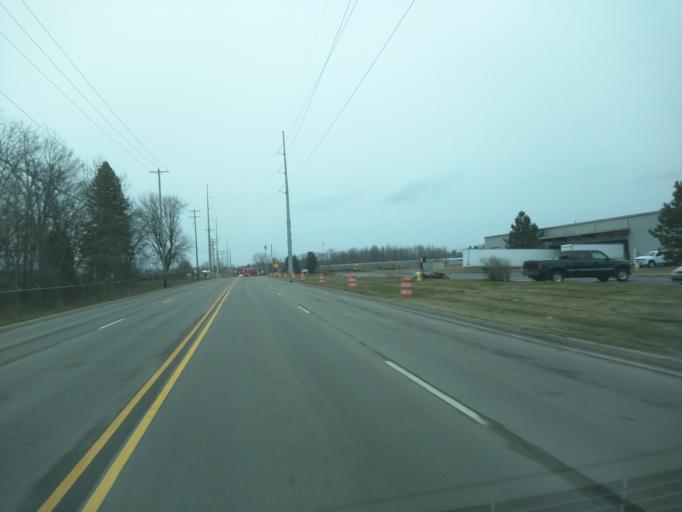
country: US
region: Michigan
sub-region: Eaton County
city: Waverly
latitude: 42.7121
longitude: -84.6151
